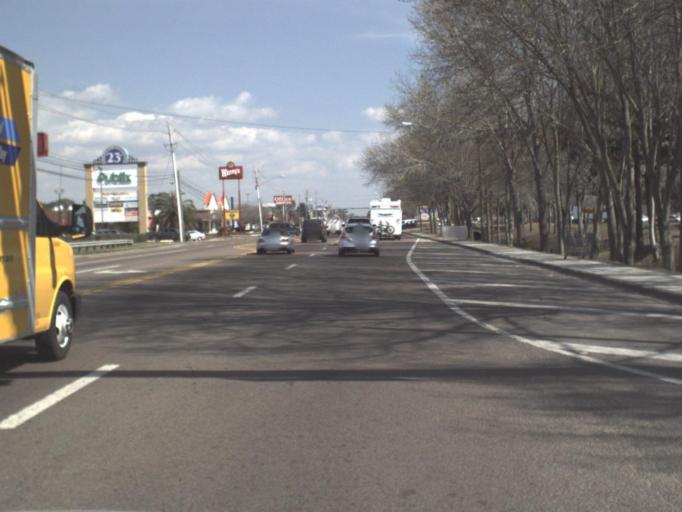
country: US
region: Florida
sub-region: Bay County
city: Pretty Bayou
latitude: 30.1897
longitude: -85.6708
